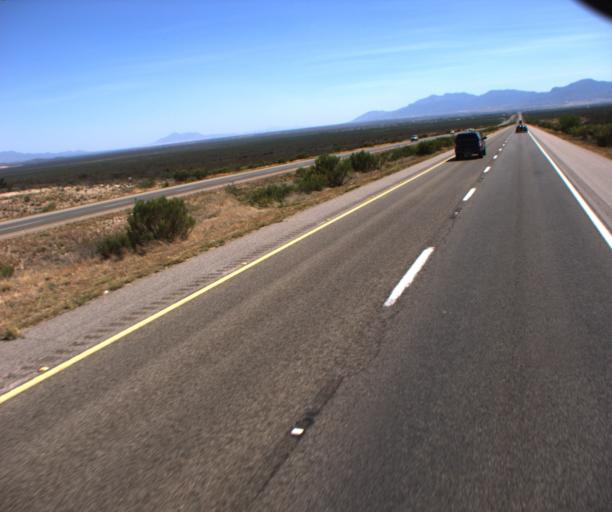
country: US
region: Arizona
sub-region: Cochise County
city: Huachuca City
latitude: 31.7683
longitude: -110.3503
